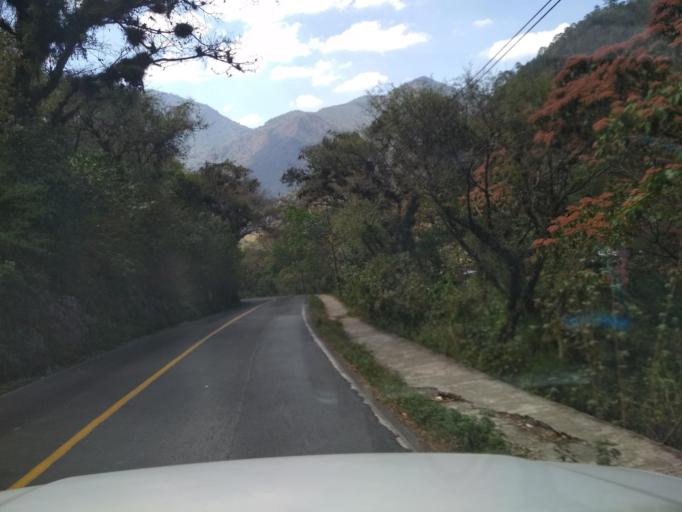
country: MX
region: Veracruz
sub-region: Tlilapan
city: Tonalixco
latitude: 18.7871
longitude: -97.0926
